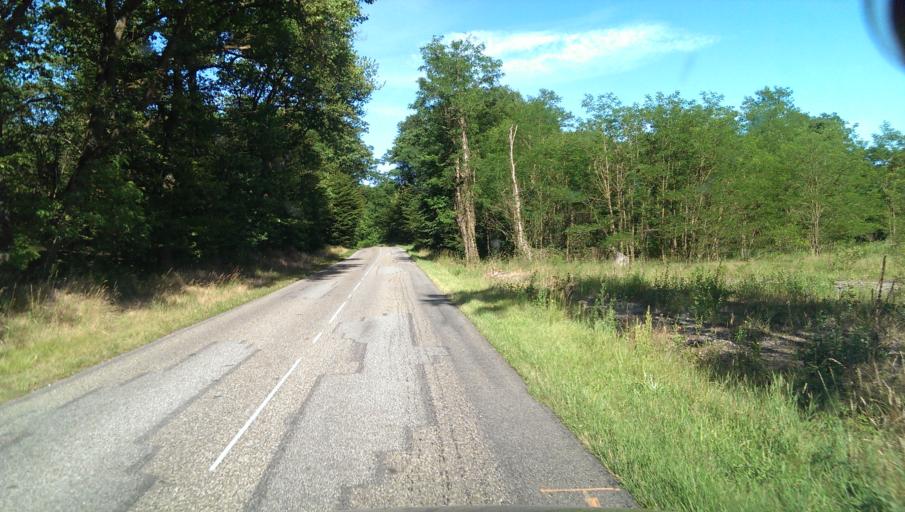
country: FR
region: Alsace
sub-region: Departement du Bas-Rhin
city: Schweighouse-sur-Moder
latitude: 48.8046
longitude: 7.7537
